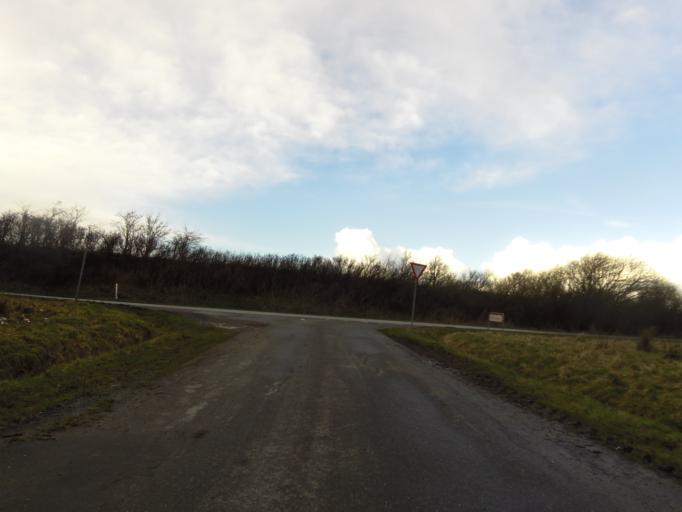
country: DK
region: South Denmark
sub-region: Haderslev Kommune
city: Gram
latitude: 55.2557
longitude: 9.0780
